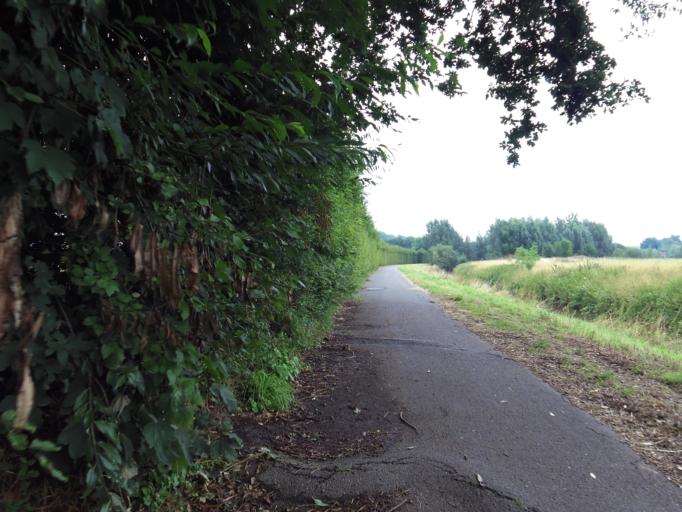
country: DE
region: North Rhine-Westphalia
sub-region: Regierungsbezirk Koln
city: Ubach-Palenberg
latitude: 50.9478
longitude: 6.1039
